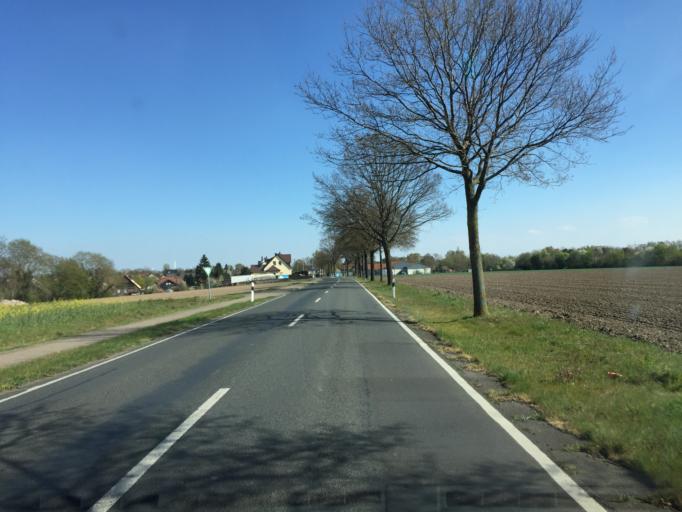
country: DE
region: Lower Saxony
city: Garbsen
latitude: 52.4031
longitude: 9.5472
